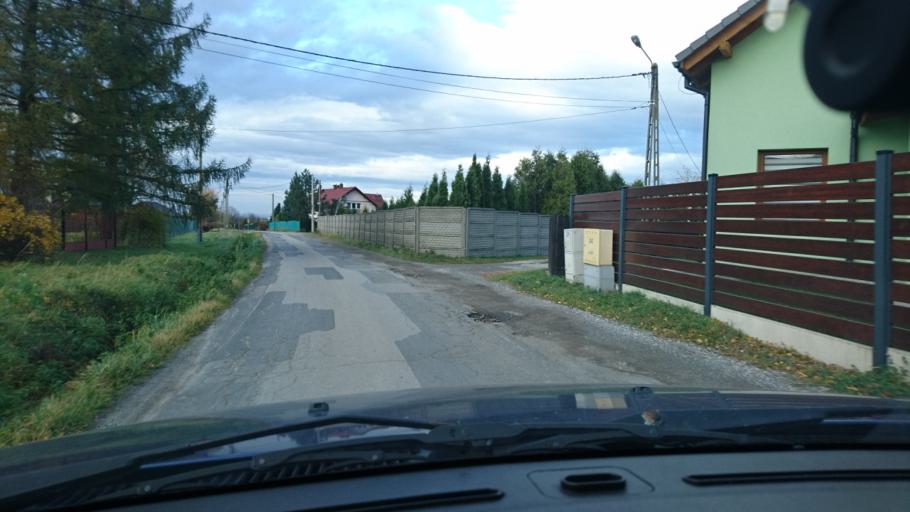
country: PL
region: Silesian Voivodeship
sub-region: Powiat bielski
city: Kozy
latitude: 49.8357
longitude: 19.1181
